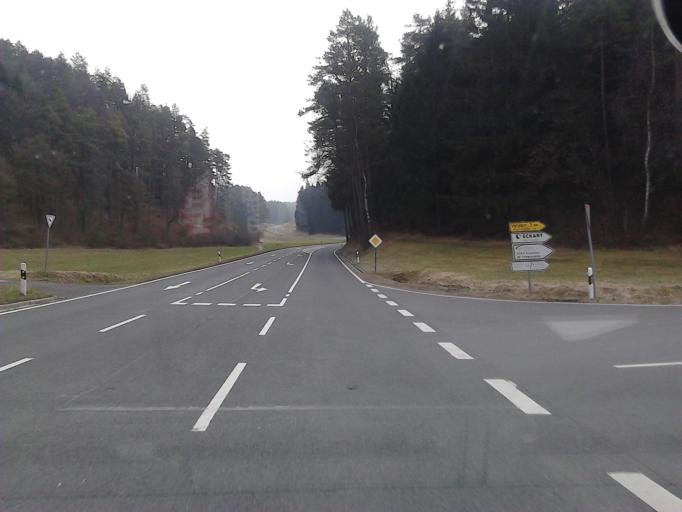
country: DE
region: Bavaria
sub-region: Regierungsbezirk Mittelfranken
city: Velden
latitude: 49.6392
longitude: 11.5168
